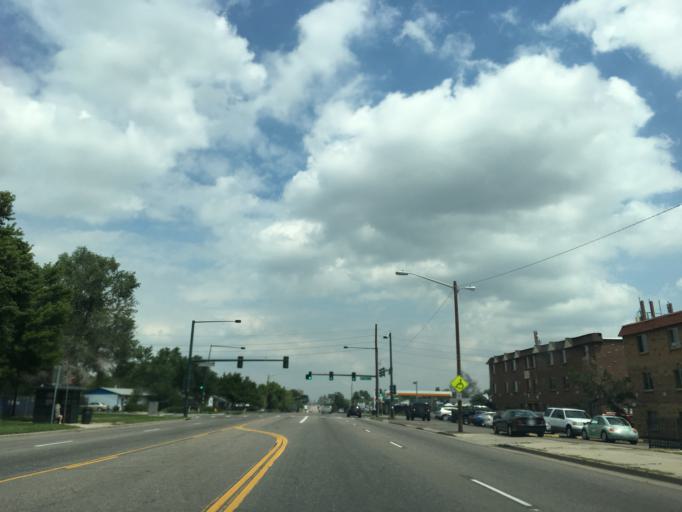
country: US
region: Colorado
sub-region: Arapahoe County
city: Sheridan
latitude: 39.6668
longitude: -105.0251
